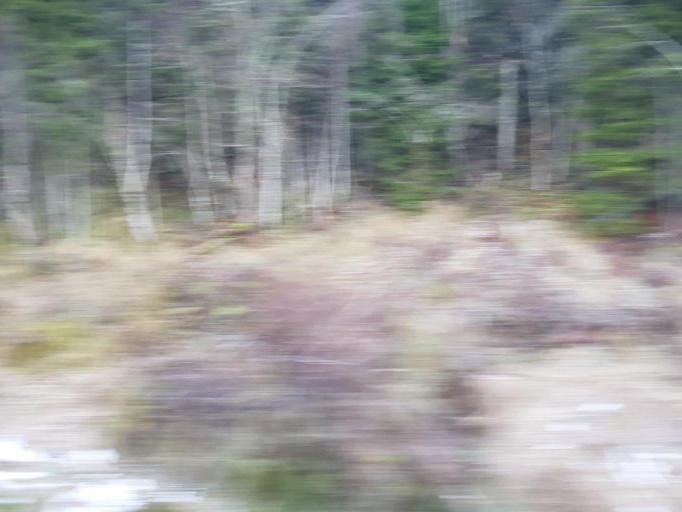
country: NO
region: Sor-Trondelag
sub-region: Midtre Gauldal
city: Storen
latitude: 63.0306
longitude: 10.2692
